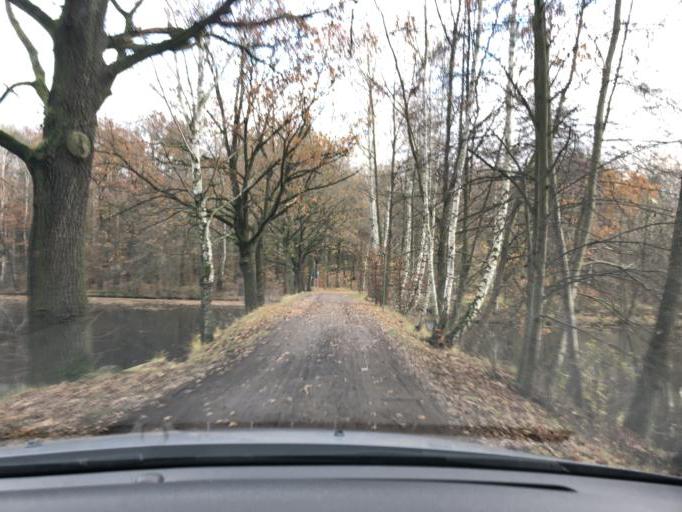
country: DE
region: Saxony
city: Mutzschen
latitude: 51.2817
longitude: 12.8986
